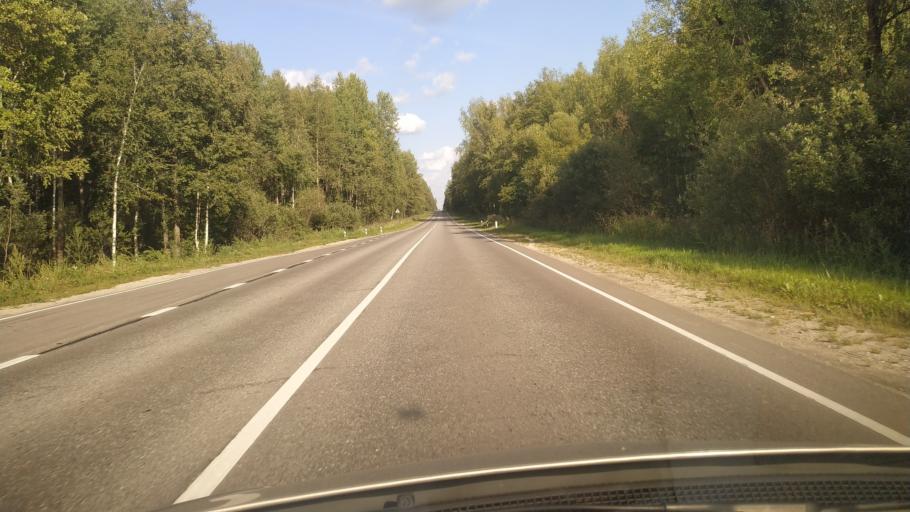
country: RU
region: Moskovskaya
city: Vereya
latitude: 55.7027
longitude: 39.1883
